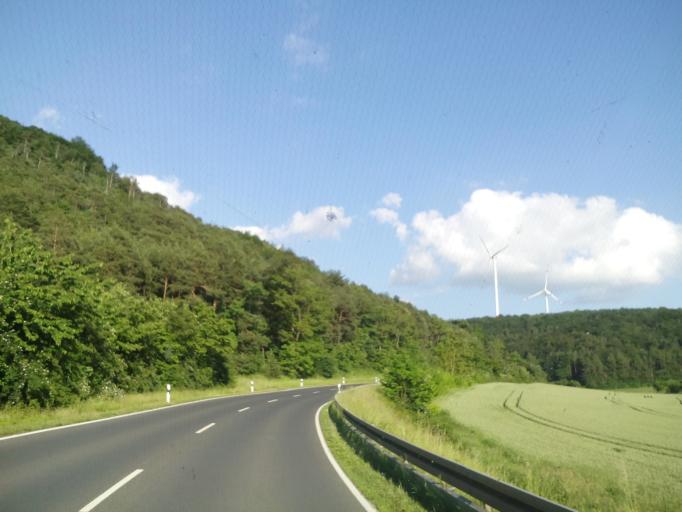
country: DE
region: Bavaria
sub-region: Regierungsbezirk Unterfranken
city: Nudlingen
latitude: 50.2261
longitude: 10.1422
